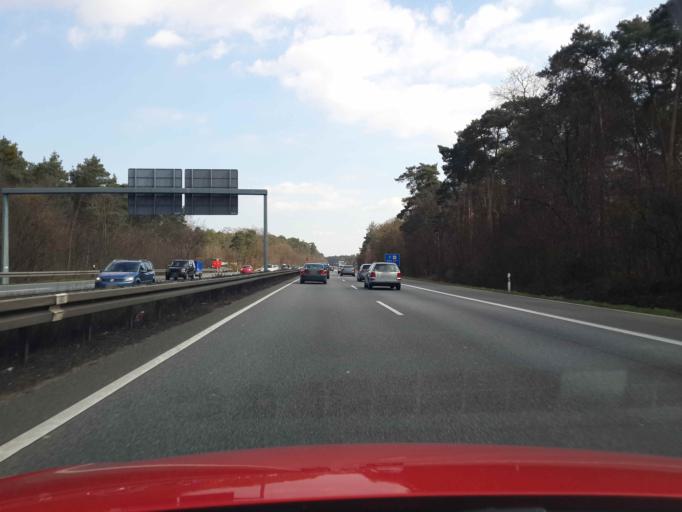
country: DE
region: Hesse
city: Raunheim
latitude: 50.0014
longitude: 8.4792
